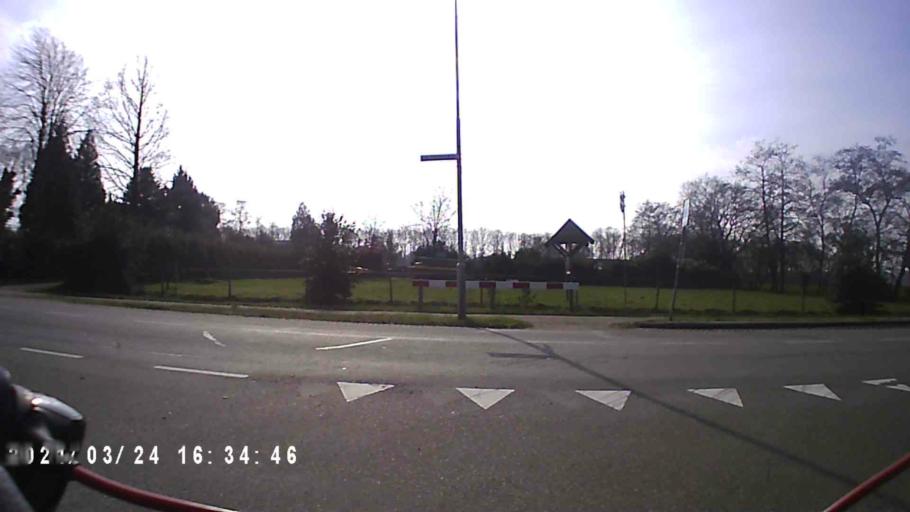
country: NL
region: Groningen
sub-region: Gemeente Leek
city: Leek
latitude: 53.0677
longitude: 6.2722
